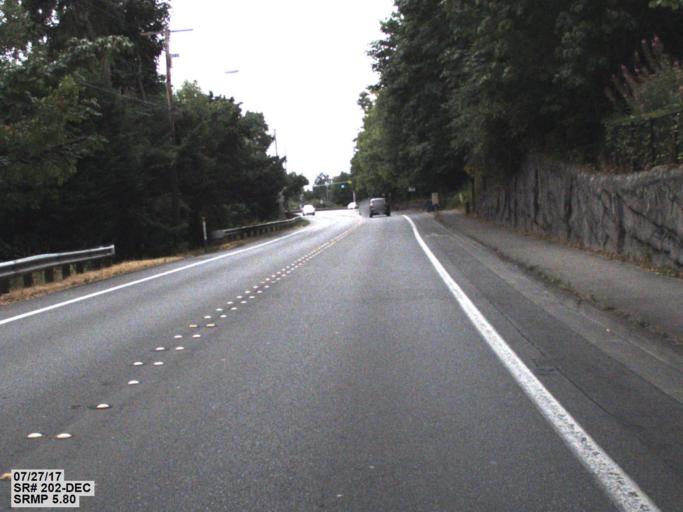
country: US
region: Washington
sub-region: King County
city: Redmond
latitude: 47.6894
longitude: -122.1295
